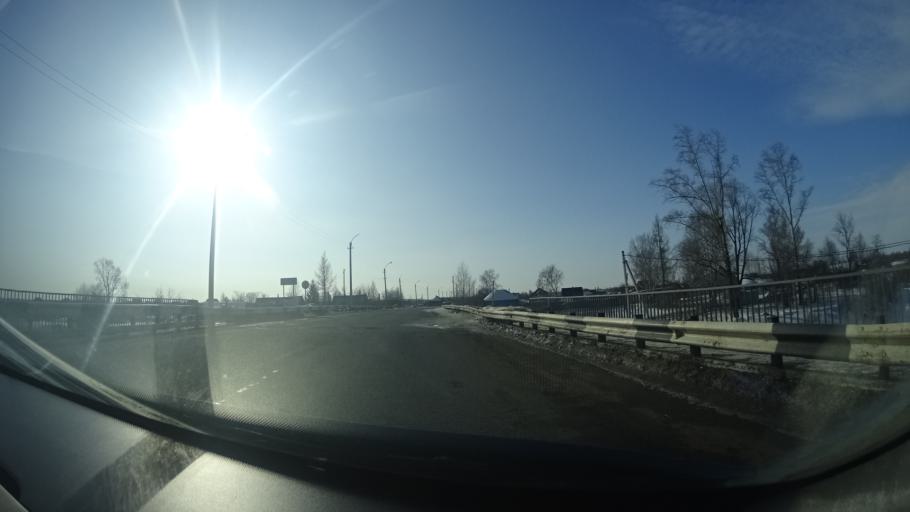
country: RU
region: Perm
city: Kuyeda
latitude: 56.4571
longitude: 55.5996
